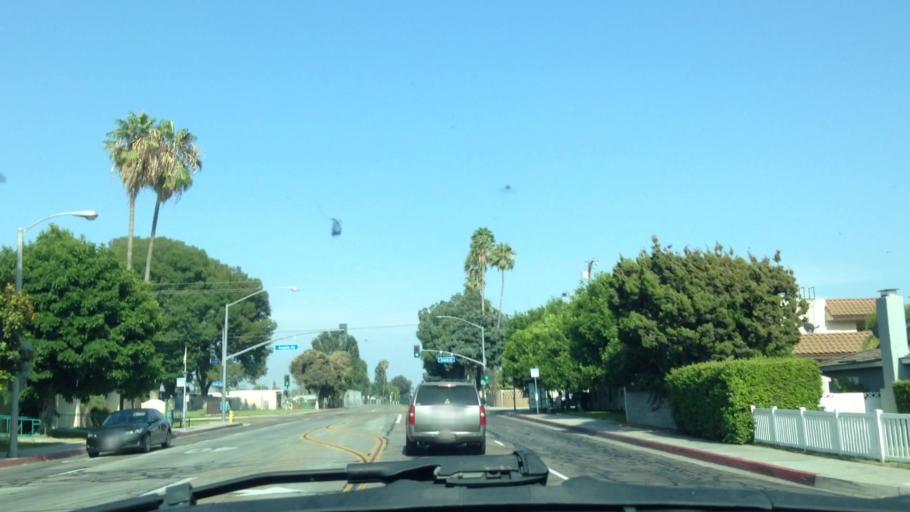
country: US
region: California
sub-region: Orange County
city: Fullerton
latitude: 33.8705
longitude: -117.8993
